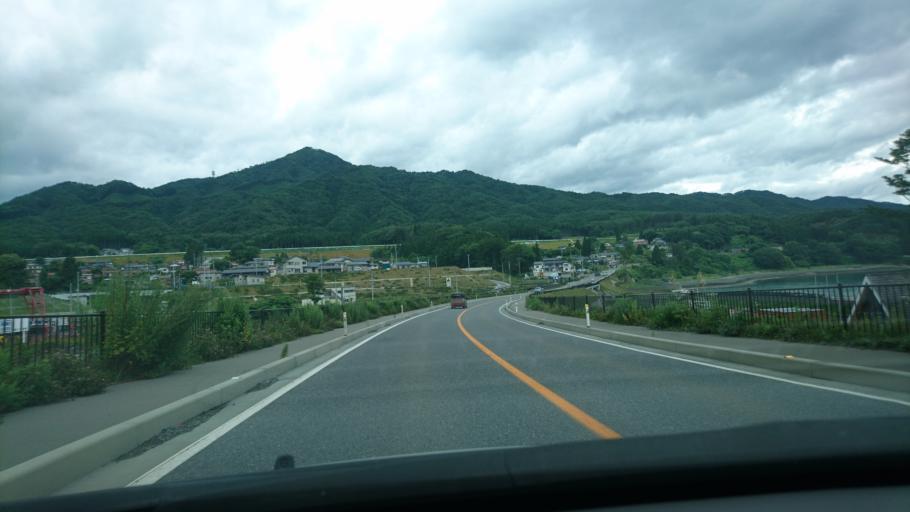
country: JP
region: Iwate
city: Otsuchi
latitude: 39.3815
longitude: 141.9377
